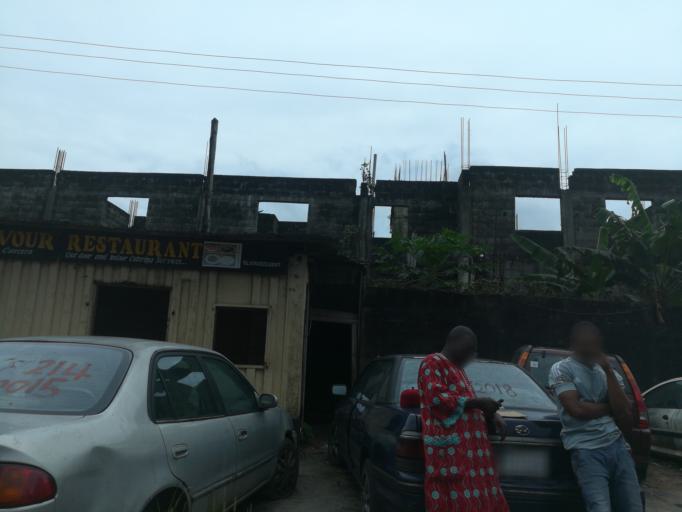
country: NG
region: Rivers
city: Port Harcourt
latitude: 4.7649
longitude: 7.0241
